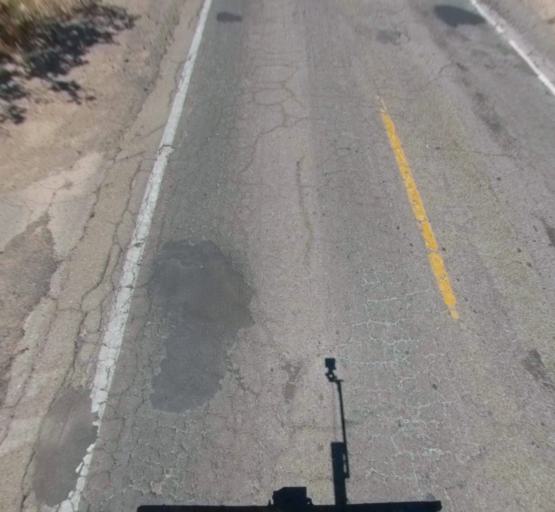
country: US
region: California
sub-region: Madera County
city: Fairmead
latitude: 37.0183
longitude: -120.1637
